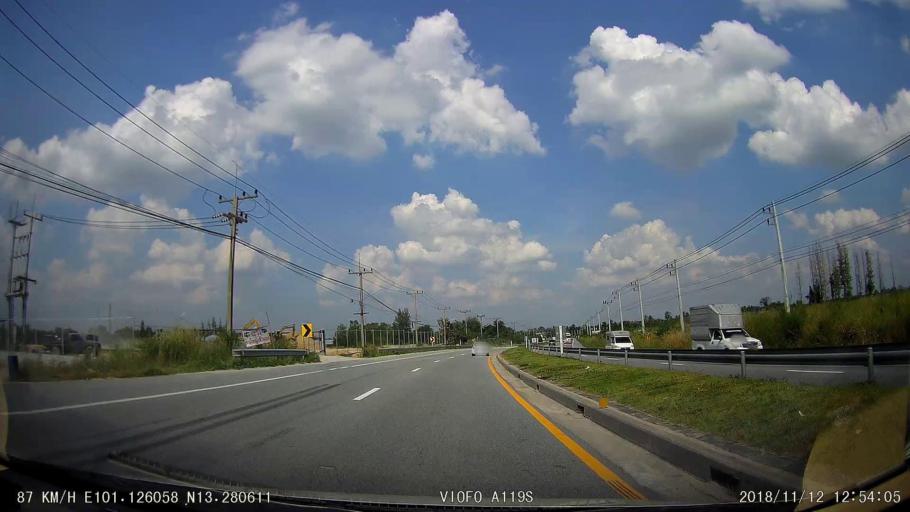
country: TH
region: Chon Buri
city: Ban Bueng
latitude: 13.2807
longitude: 101.1261
